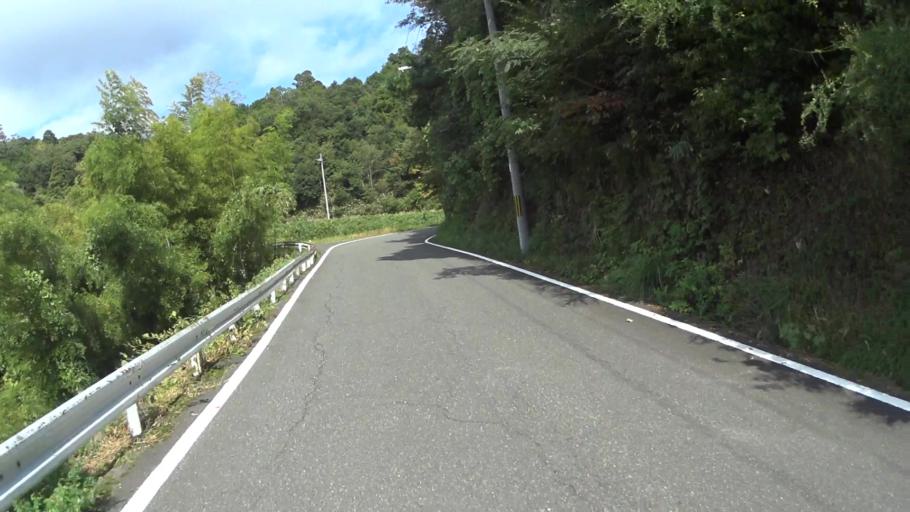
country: JP
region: Kyoto
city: Miyazu
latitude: 35.6796
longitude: 135.2677
